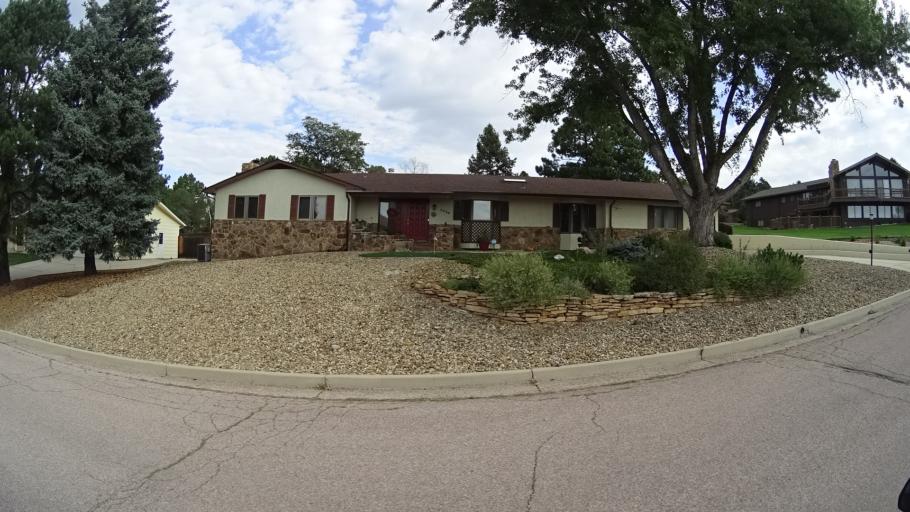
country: US
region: Colorado
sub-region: El Paso County
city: Cimarron Hills
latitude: 38.8683
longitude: -104.7418
